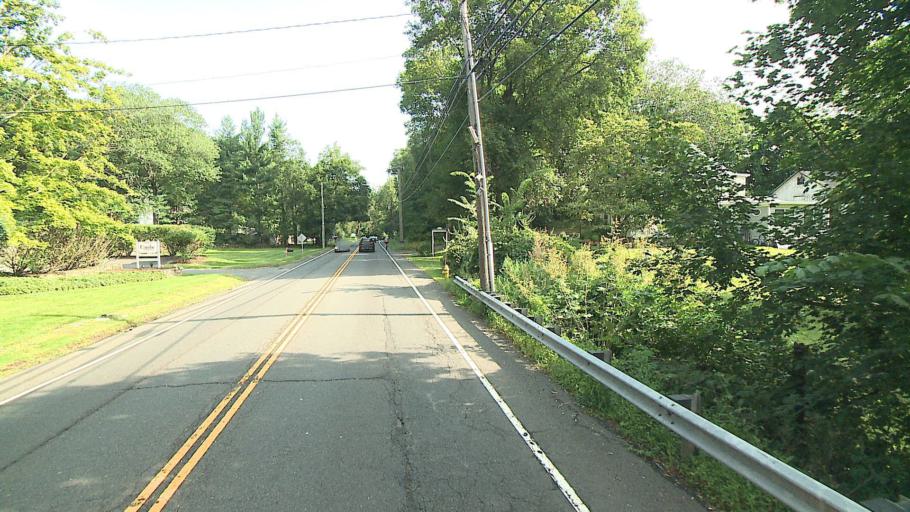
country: US
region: Connecticut
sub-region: Fairfield County
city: Wilton
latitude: 41.2242
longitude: -73.4257
